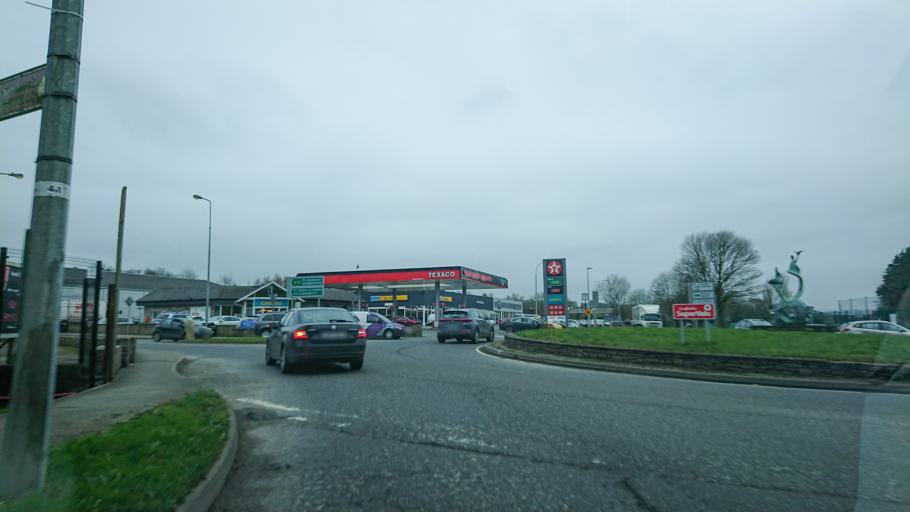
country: IE
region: Munster
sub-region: County Cork
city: Bandon
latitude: 51.7473
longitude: -8.7248
